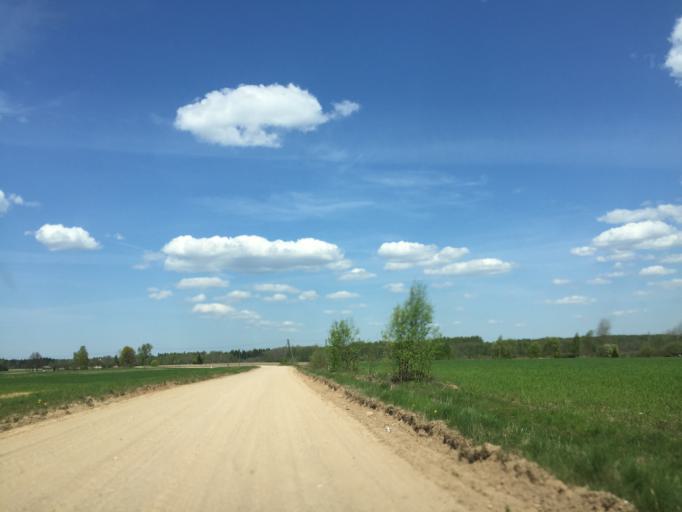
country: LV
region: Limbazu Rajons
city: Limbazi
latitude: 57.3494
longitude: 24.6506
